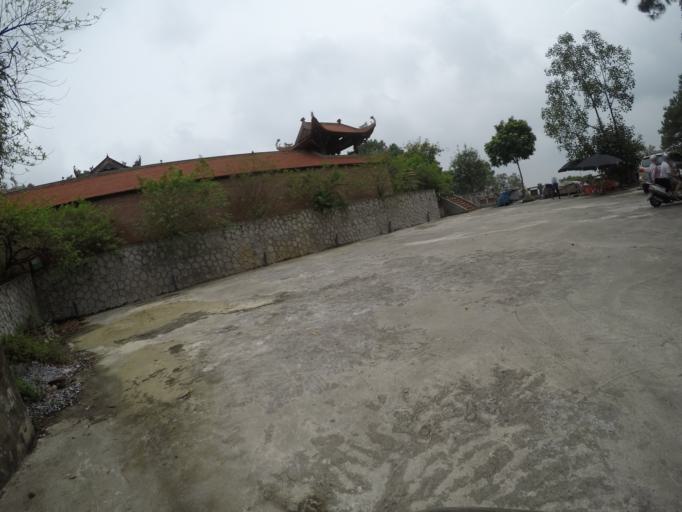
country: VN
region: Ha Noi
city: Soc Son
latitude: 21.2886
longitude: 105.8298
